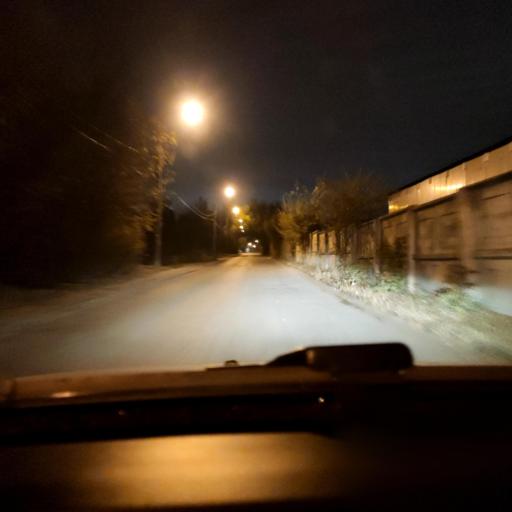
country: RU
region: Voronezj
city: Podgornoye
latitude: 51.7302
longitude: 39.1975
